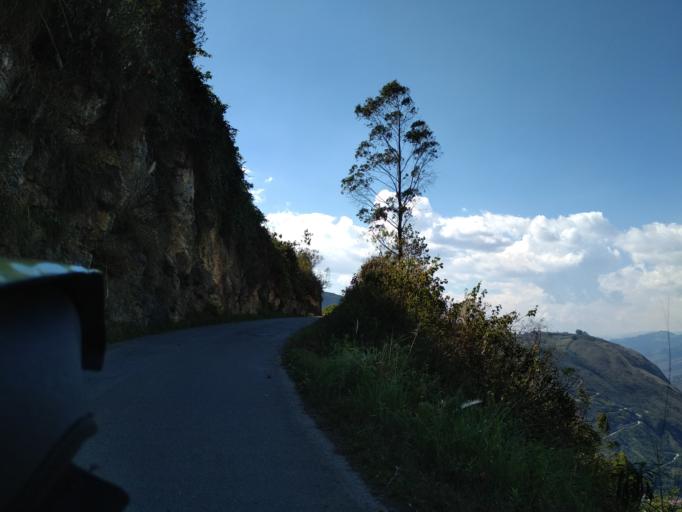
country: PE
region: Amazonas
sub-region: Provincia de Chachapoyas
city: Montevideo
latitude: -6.7189
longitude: -77.8060
